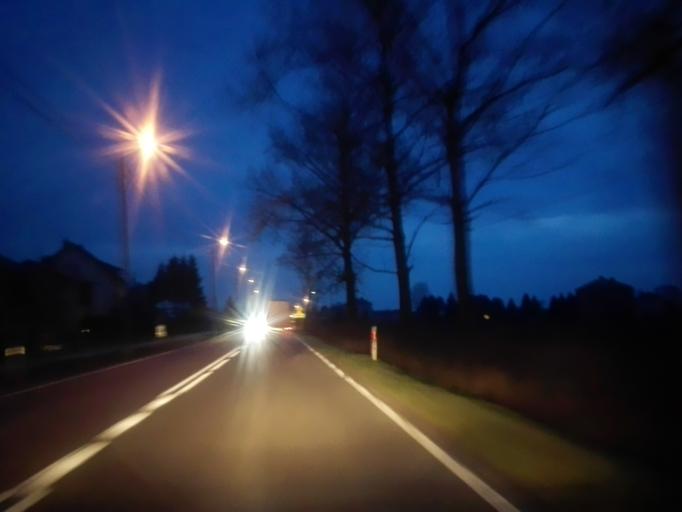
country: PL
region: Podlasie
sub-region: Powiat lomzynski
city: Sniadowo
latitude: 53.0409
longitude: 21.9875
